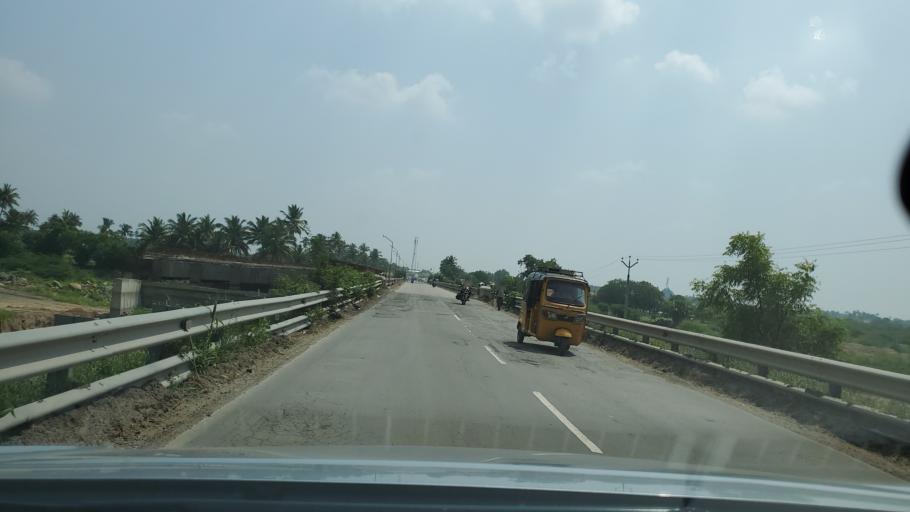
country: IN
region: Tamil Nadu
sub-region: Tiruppur
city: Dharapuram
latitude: 10.7729
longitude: 77.5096
